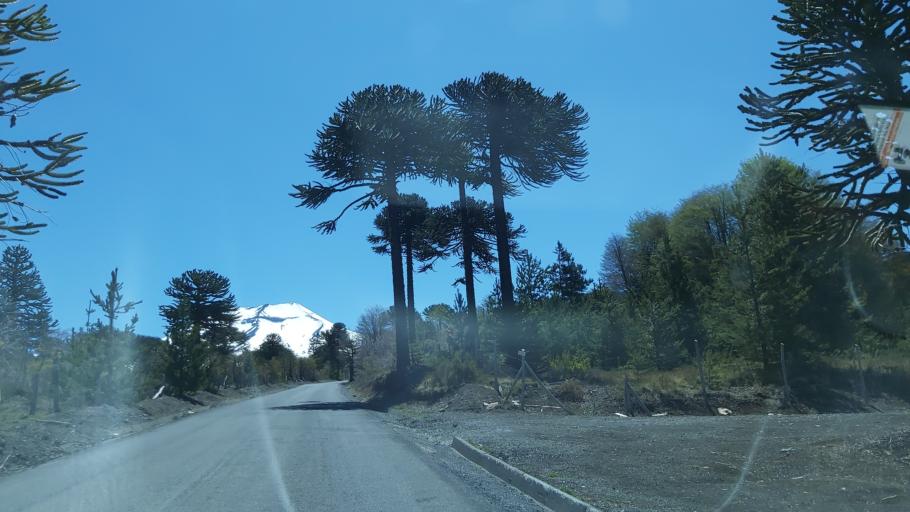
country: CL
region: Araucania
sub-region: Provincia de Cautin
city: Vilcun
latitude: -38.4340
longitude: -71.5353
